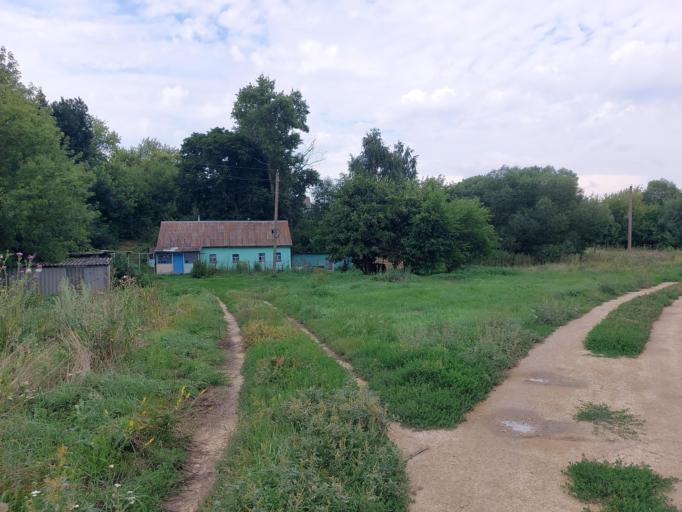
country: RU
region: Lipetsk
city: Dolgorukovo
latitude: 52.2881
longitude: 38.1867
